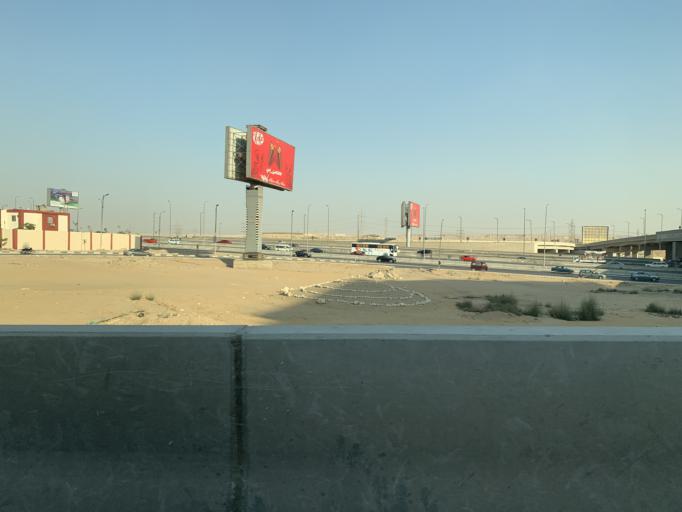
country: EG
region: Al Jizah
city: Al Hawamidiyah
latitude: 29.9799
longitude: 31.3596
